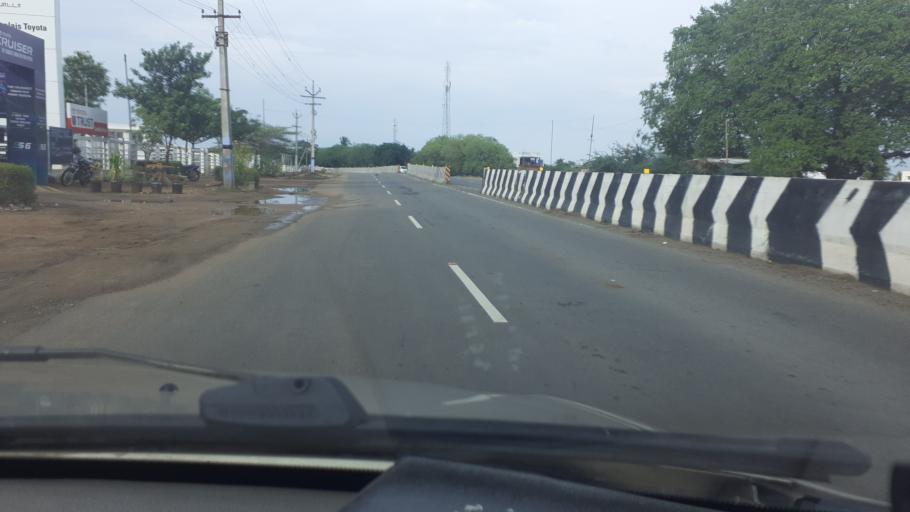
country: IN
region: Tamil Nadu
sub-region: Tirunelveli Kattabo
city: Tirunelveli
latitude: 8.6686
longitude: 77.7177
